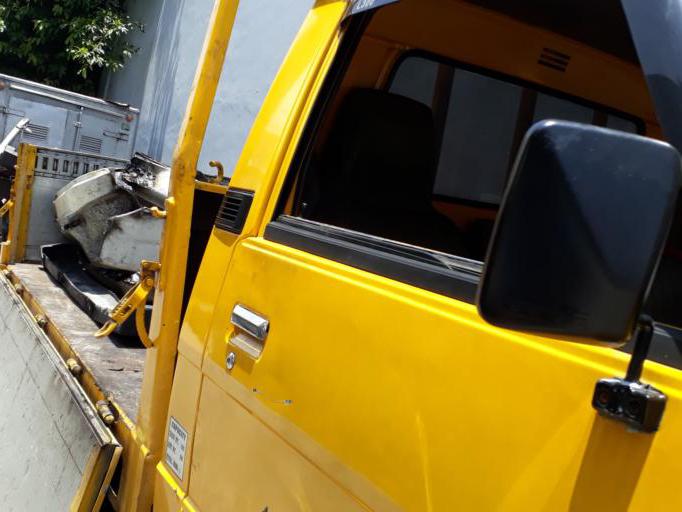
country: PH
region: Calabarzon
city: Del Monte
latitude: 14.6486
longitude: 120.9892
